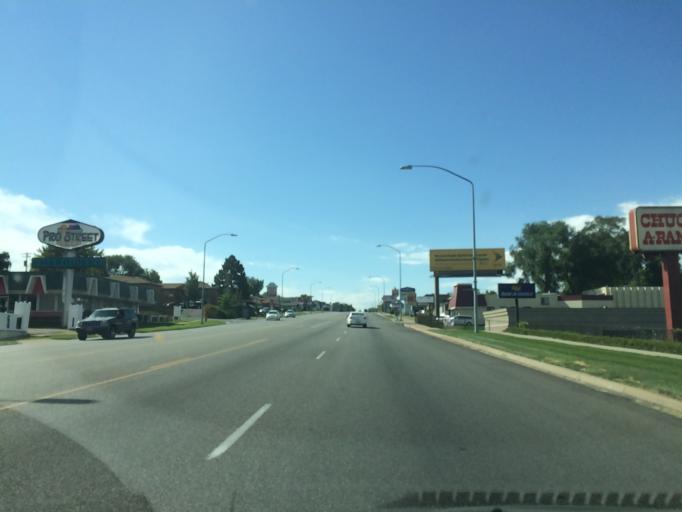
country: US
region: Utah
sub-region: Weber County
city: South Ogden
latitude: 41.1967
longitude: -111.9711
